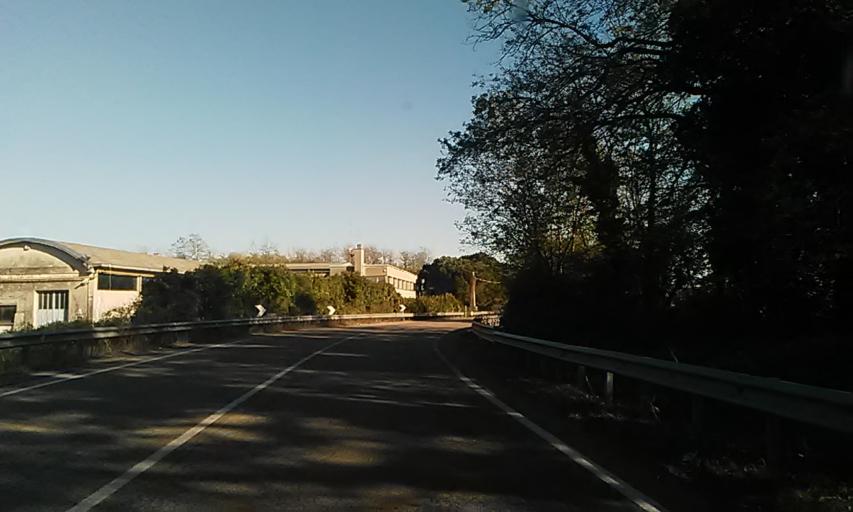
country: IT
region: Piedmont
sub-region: Provincia di Novara
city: Vaprio D'Agogna
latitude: 45.5972
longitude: 8.5365
